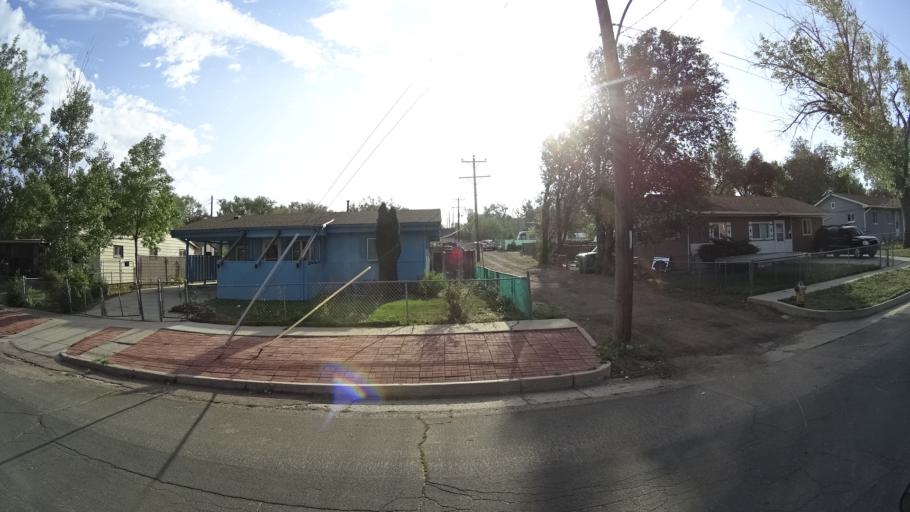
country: US
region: Colorado
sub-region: El Paso County
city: Colorado Springs
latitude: 38.8236
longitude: -104.8135
